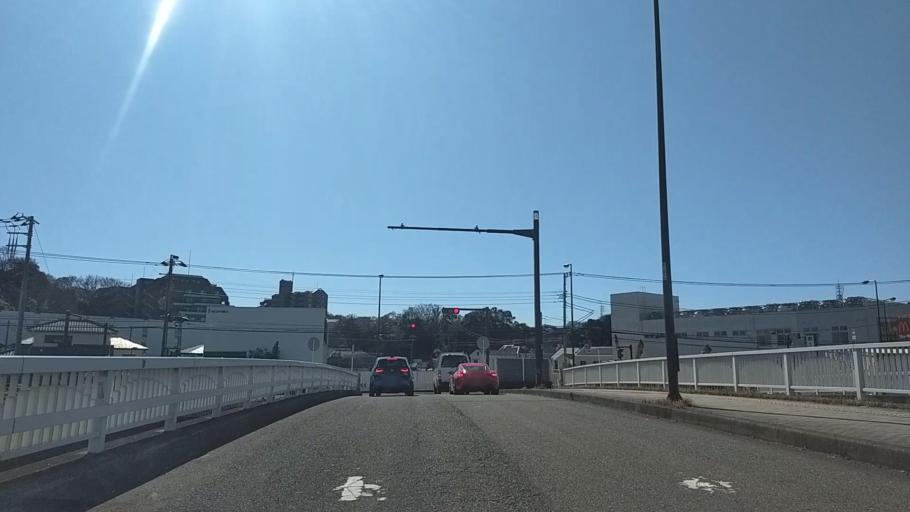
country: JP
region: Kanagawa
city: Fujisawa
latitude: 35.3331
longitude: 139.5006
